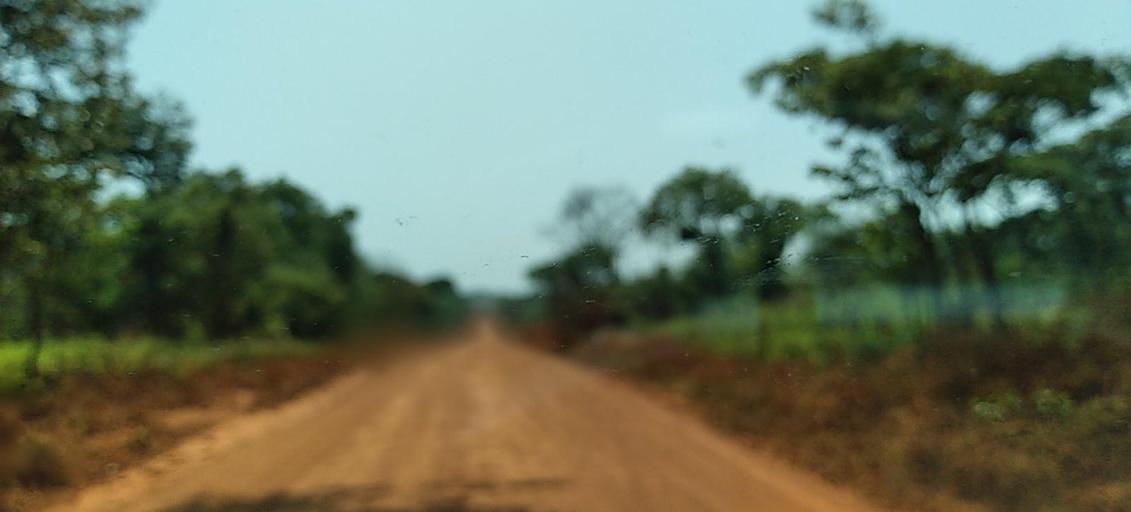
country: ZM
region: North-Western
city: Kansanshi
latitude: -11.9864
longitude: 26.8509
